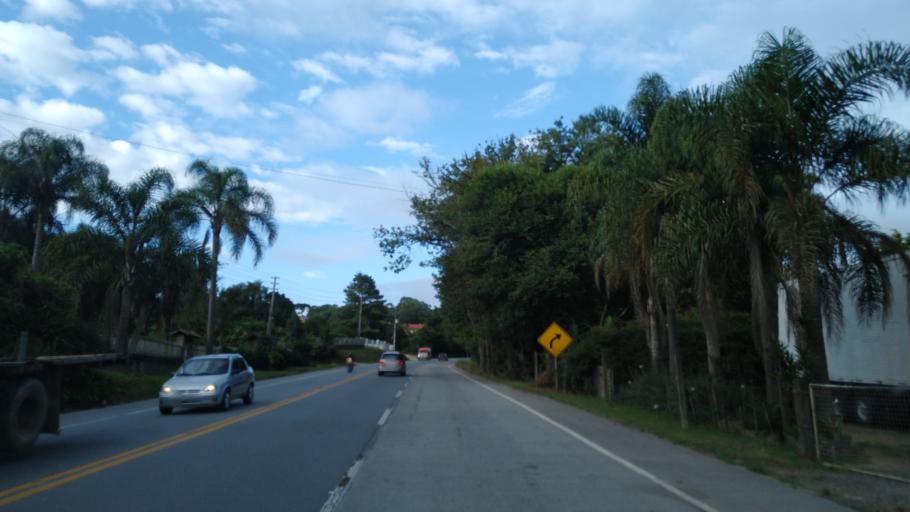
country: BR
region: Santa Catarina
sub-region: Sao Bento Do Sul
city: Sao Bento do Sul
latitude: -26.2421
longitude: -49.4378
